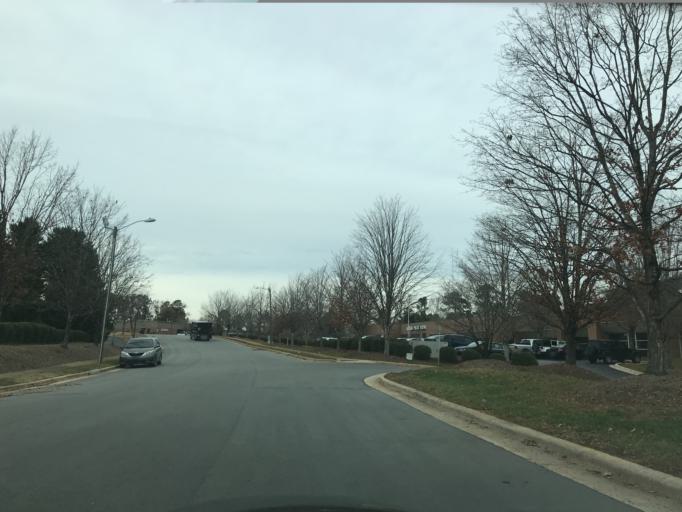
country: US
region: North Carolina
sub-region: Wake County
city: West Raleigh
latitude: 35.7910
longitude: -78.7018
